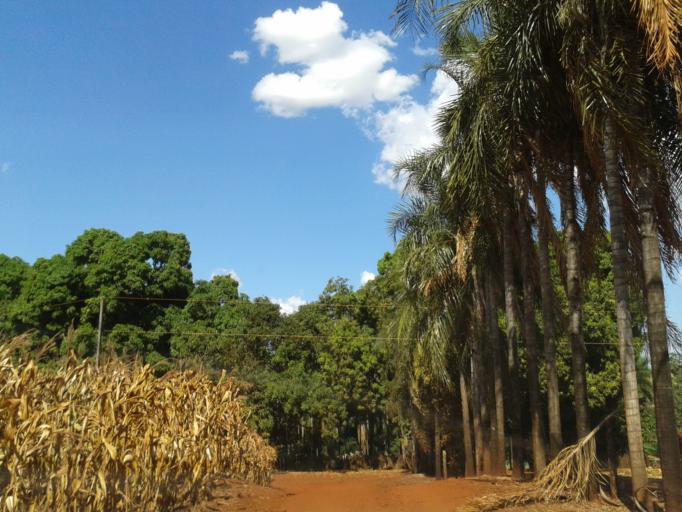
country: BR
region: Minas Gerais
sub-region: Capinopolis
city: Capinopolis
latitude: -18.6284
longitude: -49.4769
